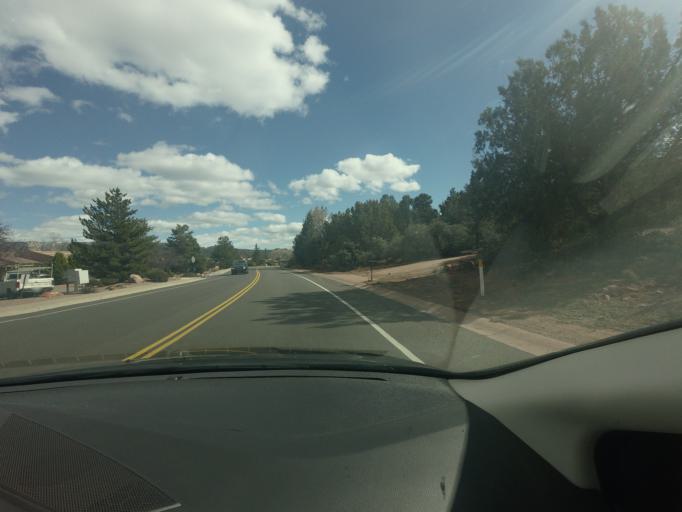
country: US
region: Arizona
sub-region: Yavapai County
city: West Sedona
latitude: 34.8659
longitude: -111.8183
